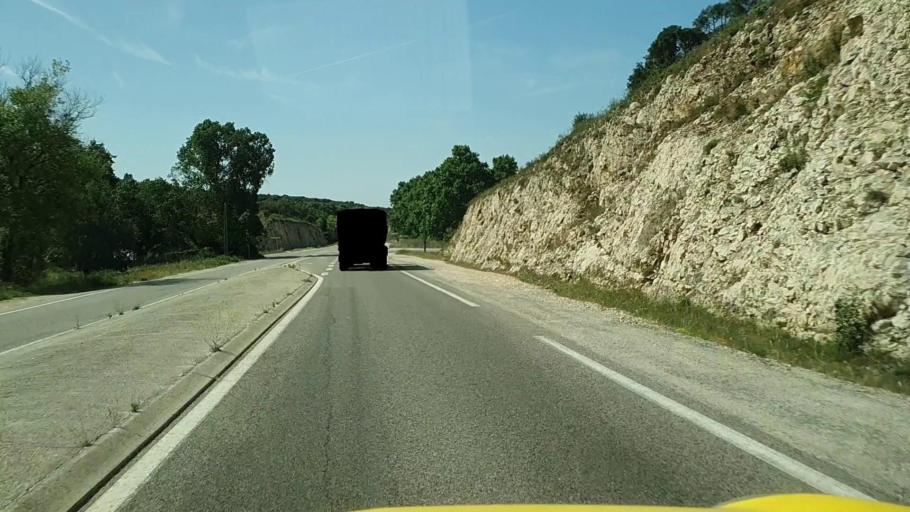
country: FR
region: Languedoc-Roussillon
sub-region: Departement du Gard
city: Connaux
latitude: 44.0297
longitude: 4.5815
